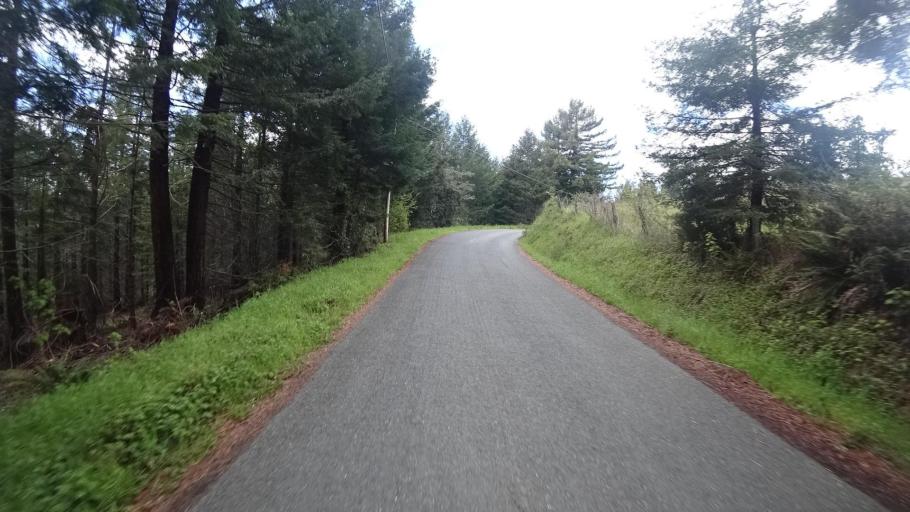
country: US
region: California
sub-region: Humboldt County
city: Blue Lake
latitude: 40.8569
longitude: -123.9337
